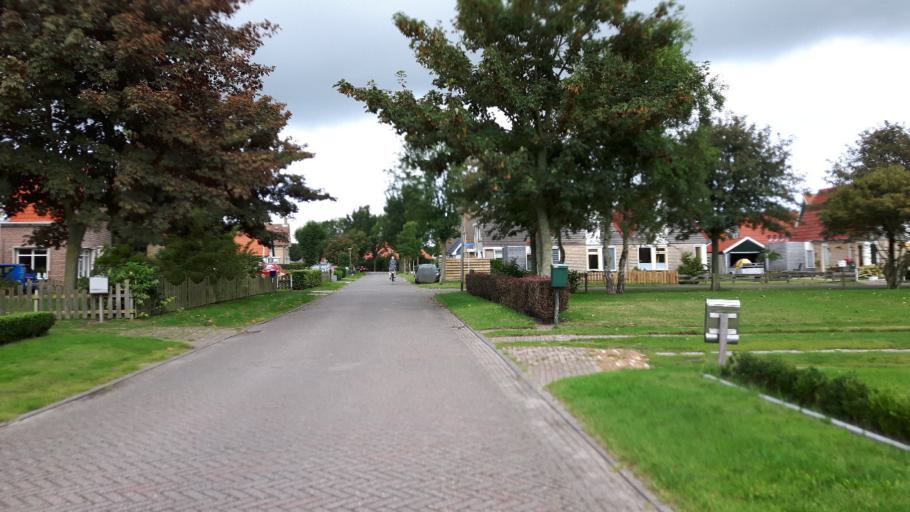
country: NL
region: Friesland
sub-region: Gemeente Ameland
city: Hollum
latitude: 53.4391
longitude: 5.6416
